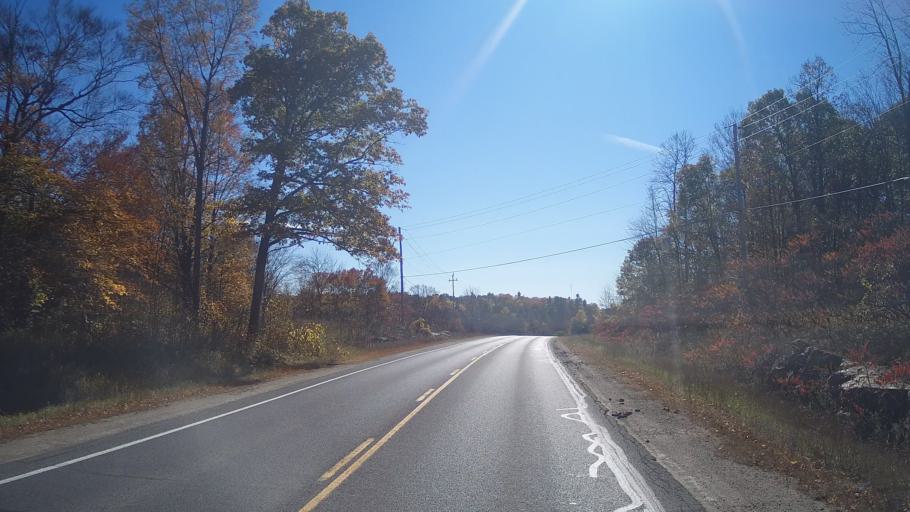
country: CA
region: Ontario
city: Kingston
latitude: 44.5561
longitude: -76.6734
